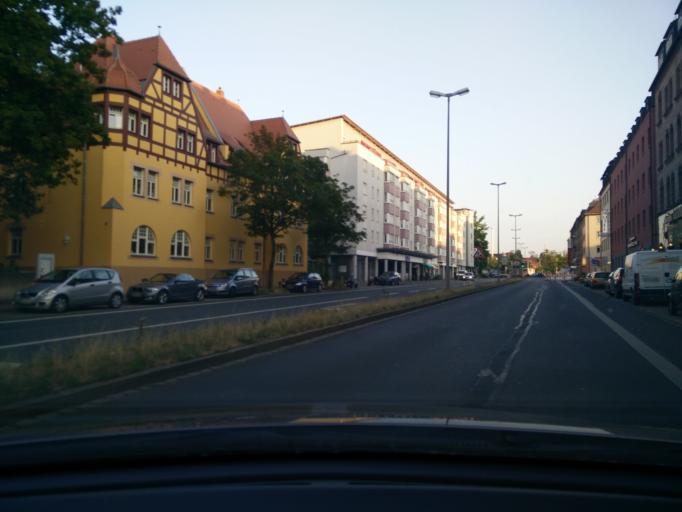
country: DE
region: Bavaria
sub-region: Regierungsbezirk Mittelfranken
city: Nuernberg
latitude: 49.4316
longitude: 11.0864
